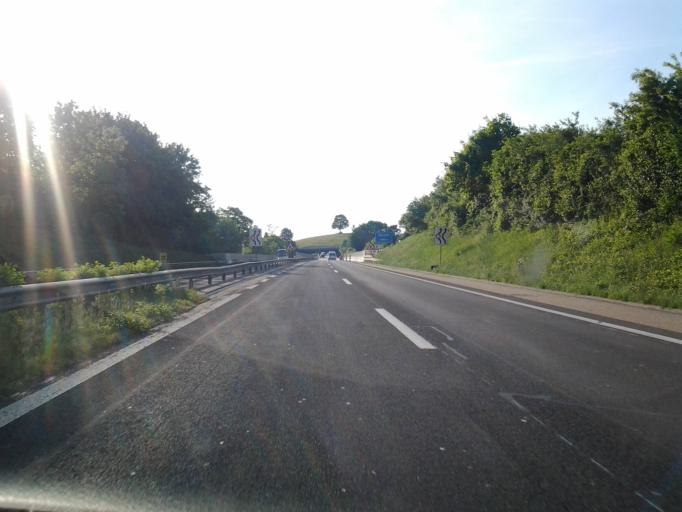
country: CH
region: Lucerne
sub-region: Sursee District
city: Schenkon
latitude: 47.1734
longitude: 8.1300
